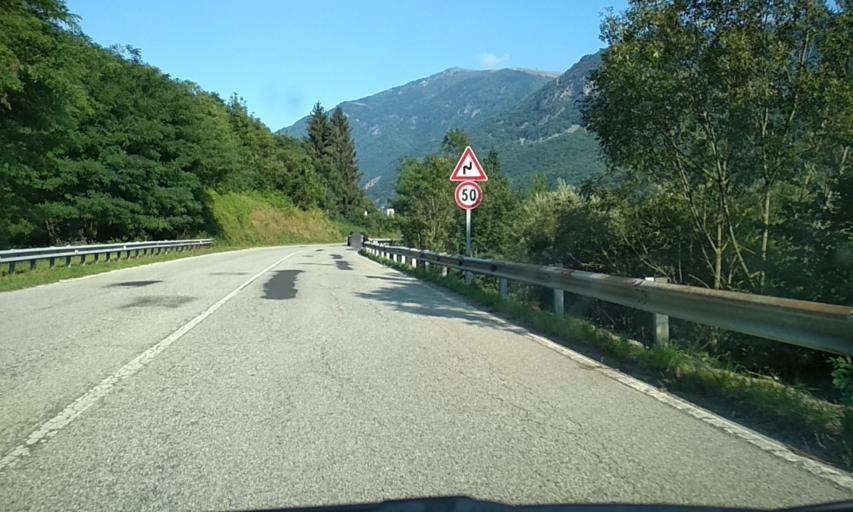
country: IT
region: Piedmont
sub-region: Provincia di Torino
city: Ribordone
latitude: 45.4073
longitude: 7.4992
